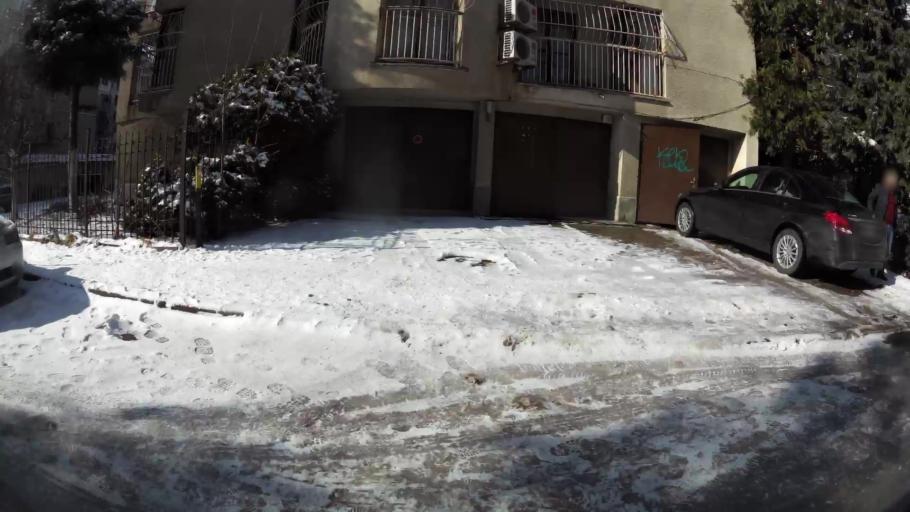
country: BG
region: Sofia-Capital
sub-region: Stolichna Obshtina
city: Sofia
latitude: 42.6632
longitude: 23.3153
